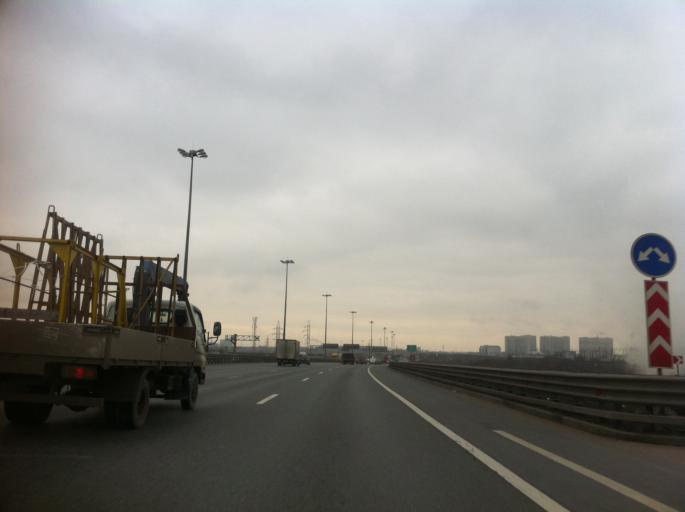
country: RU
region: St.-Petersburg
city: Shushary
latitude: 59.8152
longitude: 30.3693
